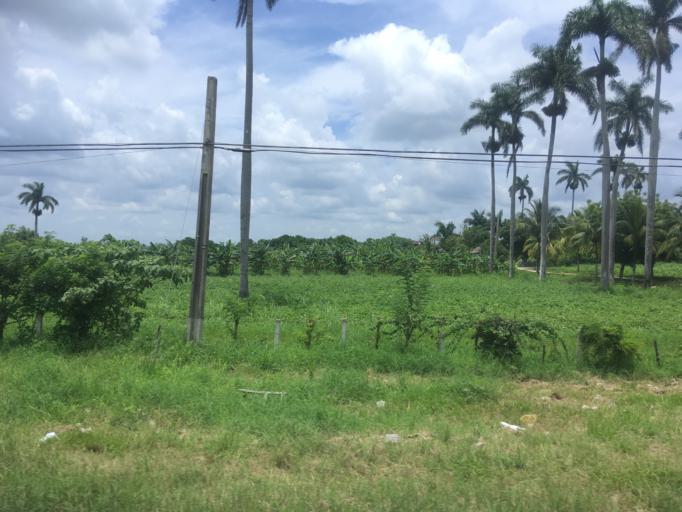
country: CU
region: Villa Clara
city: Esperanza
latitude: 22.4128
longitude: -80.0391
